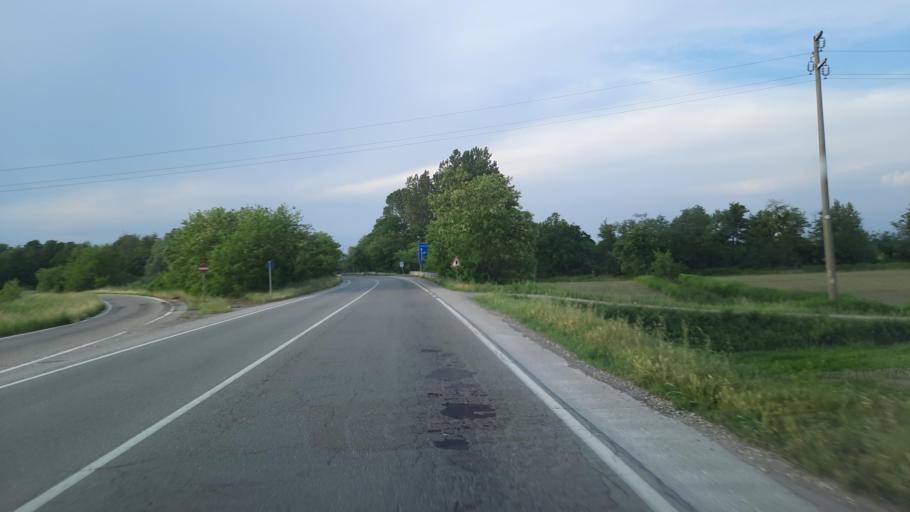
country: IT
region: Lombardy
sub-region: Provincia di Pavia
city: Tromello
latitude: 45.2117
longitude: 8.8590
